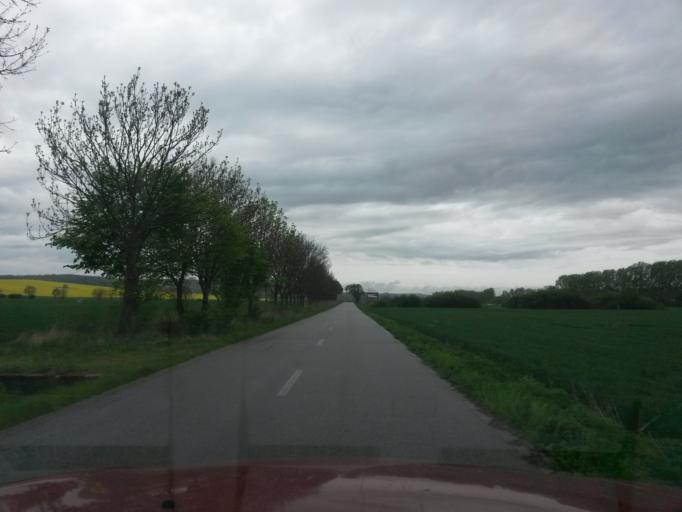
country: HU
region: Borsod-Abauj-Zemplen
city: Gonc
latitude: 48.5422
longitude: 21.2109
